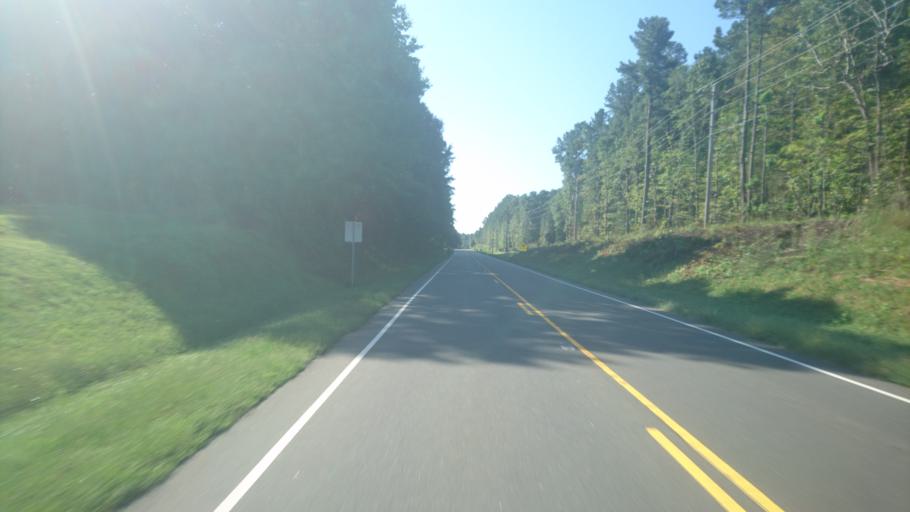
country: US
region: North Carolina
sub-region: Orange County
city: Hillsborough
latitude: 36.0308
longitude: -79.0807
